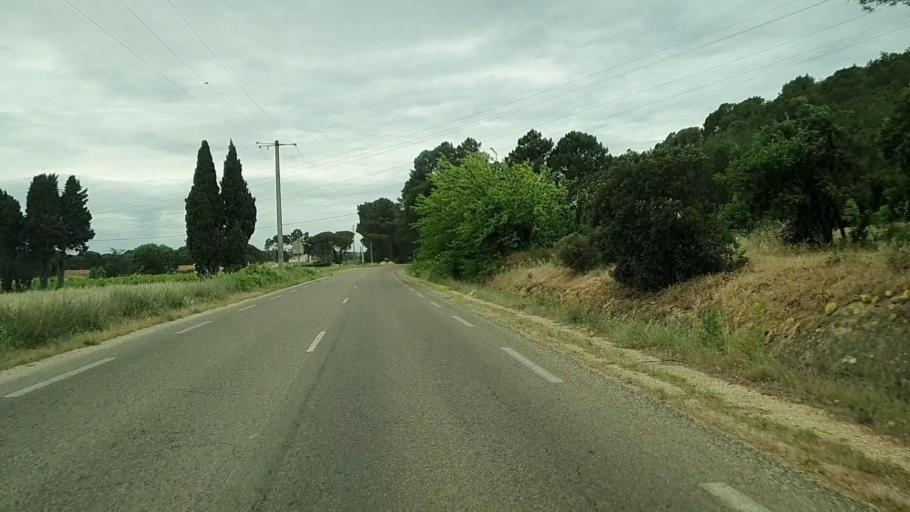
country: FR
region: Languedoc-Roussillon
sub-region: Departement du Gard
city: Tresques
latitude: 44.1213
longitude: 4.5976
